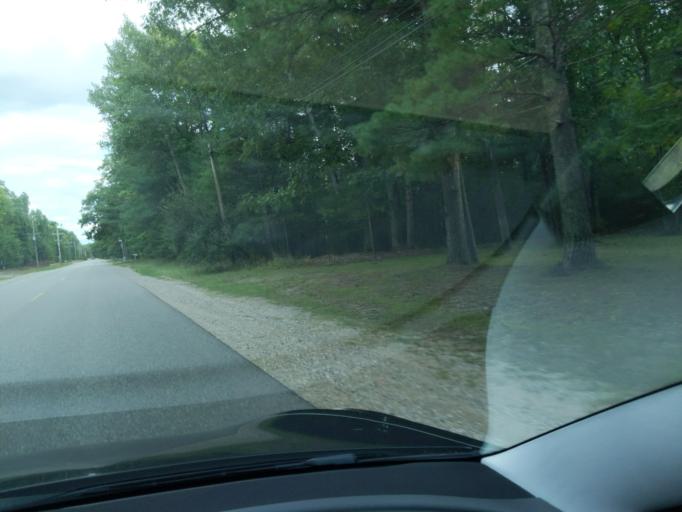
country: US
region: Michigan
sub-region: Kalkaska County
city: Rapid City
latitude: 44.8505
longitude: -85.3140
